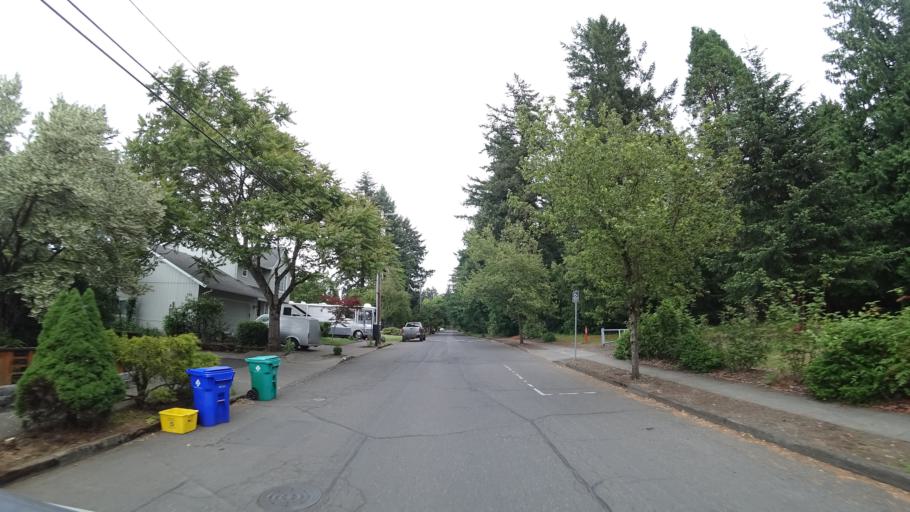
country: US
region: Oregon
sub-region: Clackamas County
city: Happy Valley
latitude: 45.4932
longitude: -122.5150
